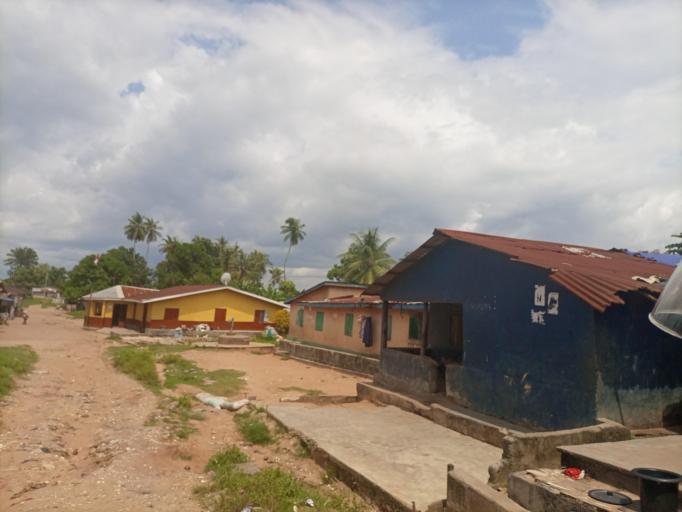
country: SL
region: Western Area
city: Freetown
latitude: 8.5241
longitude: -13.1468
